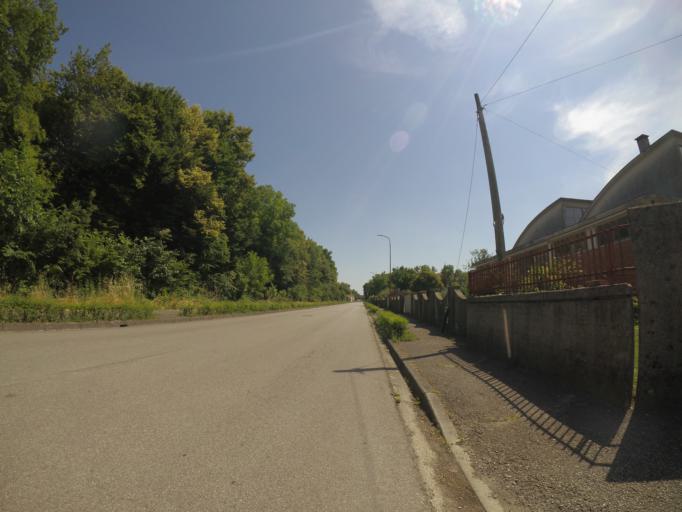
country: IT
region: Friuli Venezia Giulia
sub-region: Provincia di Udine
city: Camino al Tagliamento
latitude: 45.9307
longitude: 12.9448
